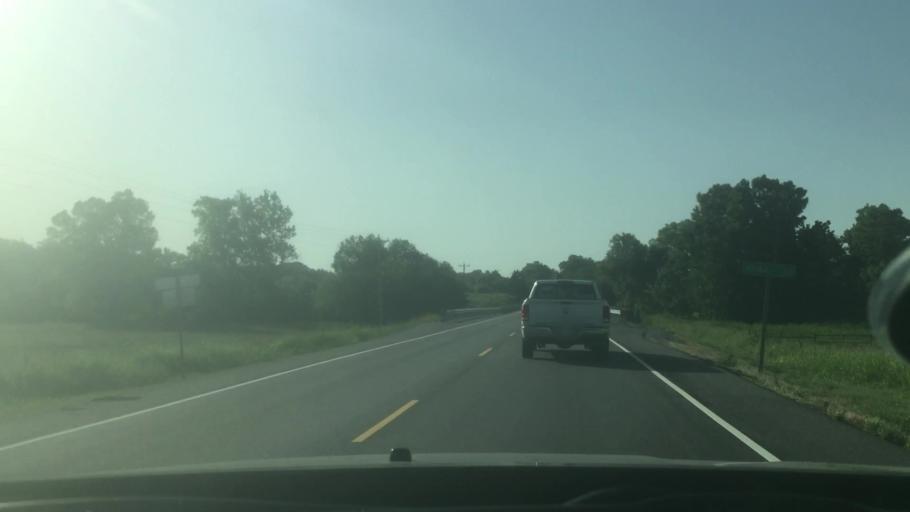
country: US
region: Oklahoma
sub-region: Bryan County
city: Durant
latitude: 34.1703
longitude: -96.4083
